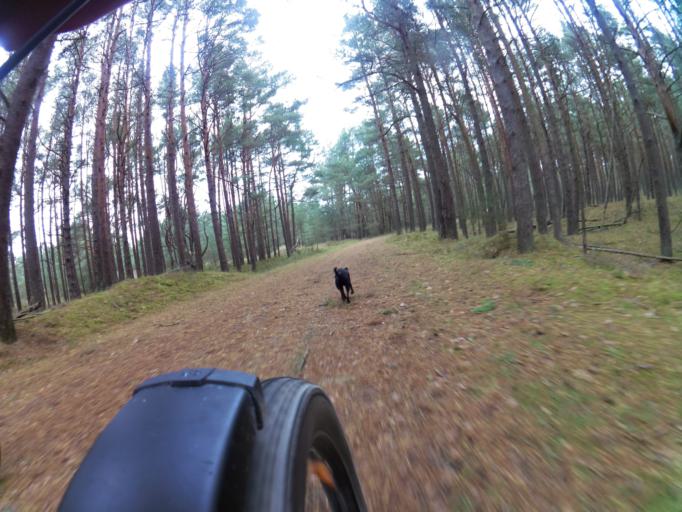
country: PL
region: Pomeranian Voivodeship
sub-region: Powiat leborski
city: Leba
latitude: 54.7694
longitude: 17.5970
